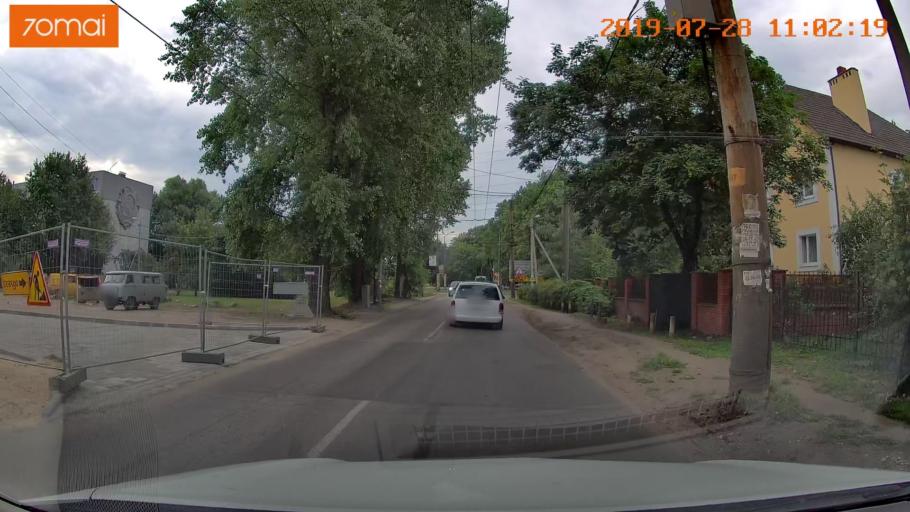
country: RU
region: Kaliningrad
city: Vzmorye
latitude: 54.7163
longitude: 20.3704
